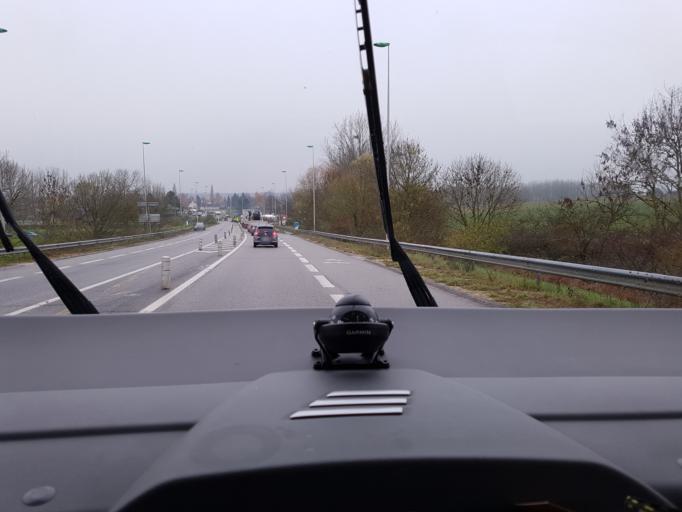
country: FR
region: Haute-Normandie
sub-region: Departement de la Seine-Maritime
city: Caudebec-en-Caux
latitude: 49.5125
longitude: 0.7418
